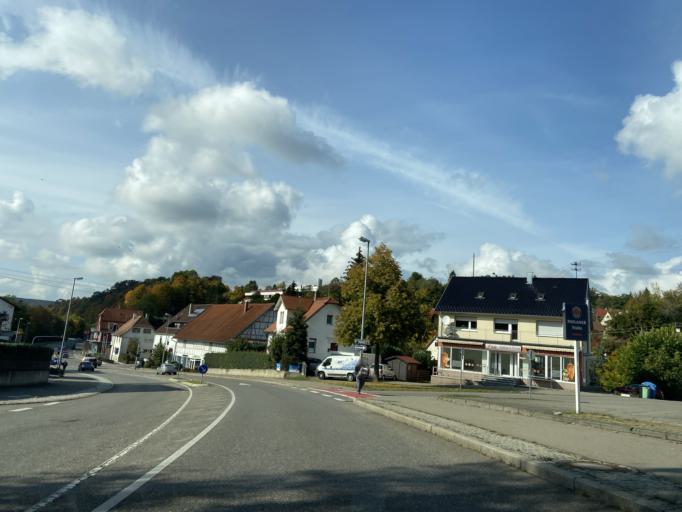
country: DE
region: Baden-Wuerttemberg
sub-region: Tuebingen Region
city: Sigmaringen
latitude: 48.0904
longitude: 9.2282
